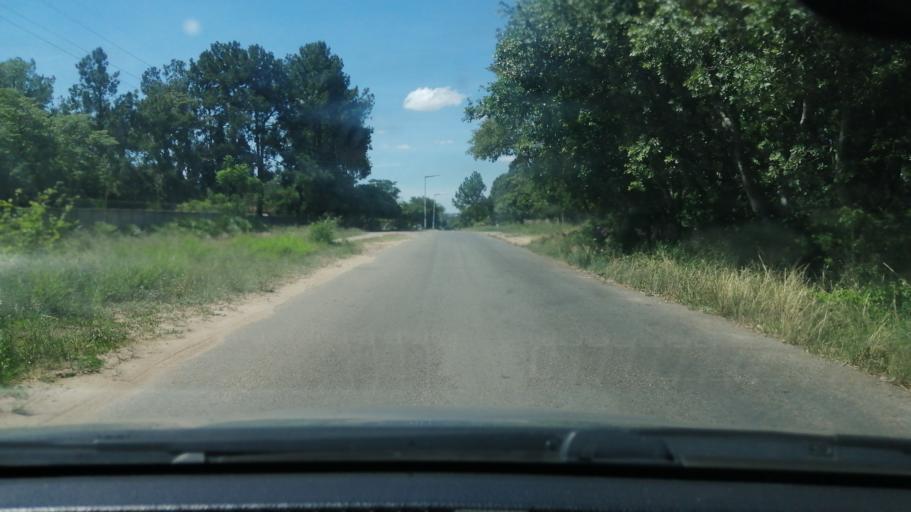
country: ZW
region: Harare
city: Epworth
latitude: -17.8263
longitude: 31.1255
